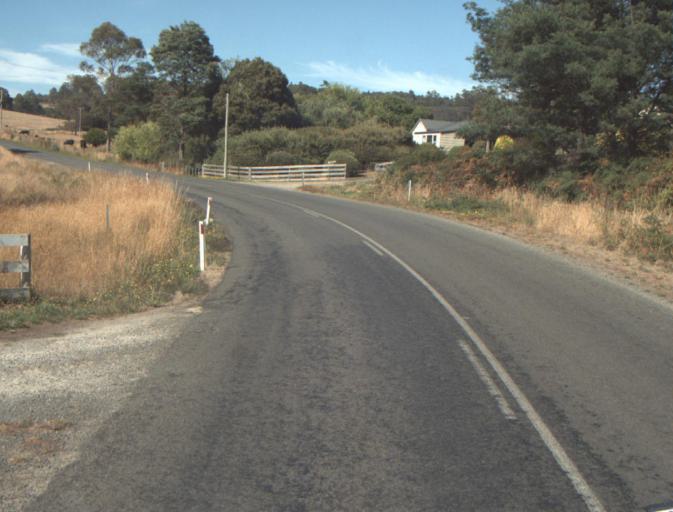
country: AU
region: Tasmania
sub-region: Launceston
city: Mayfield
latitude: -41.1921
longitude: 147.2210
